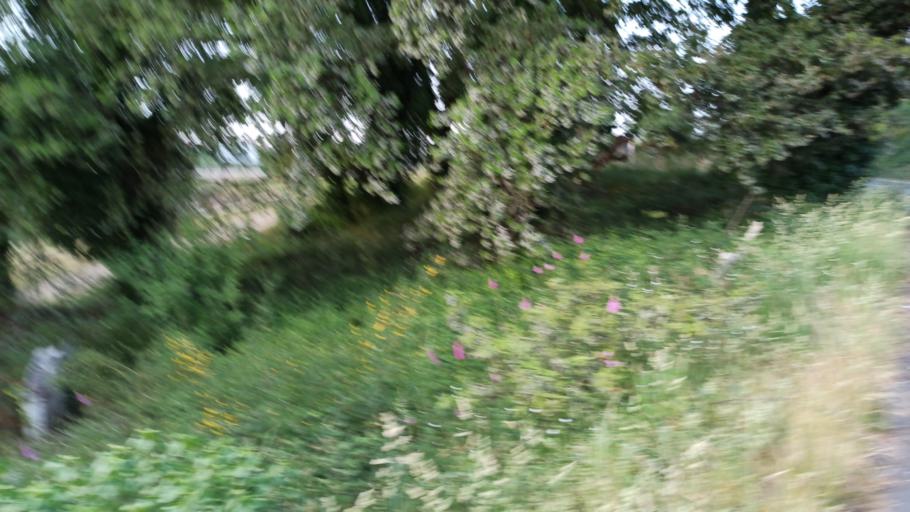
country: ES
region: Galicia
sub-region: Provincia da Coruna
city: Negreira
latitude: 42.9187
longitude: -8.7483
